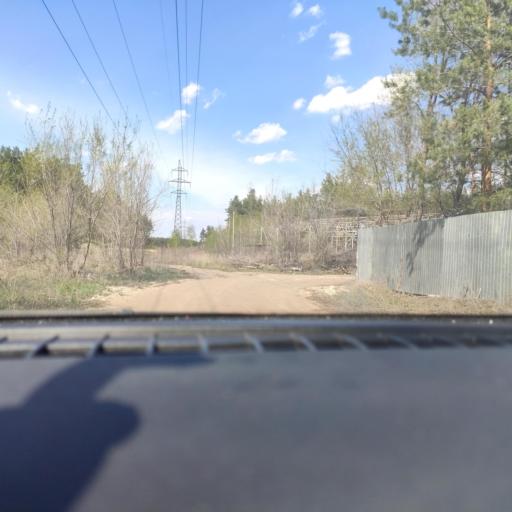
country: RU
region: Voronezj
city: Maslovka
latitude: 51.5948
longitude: 39.2158
